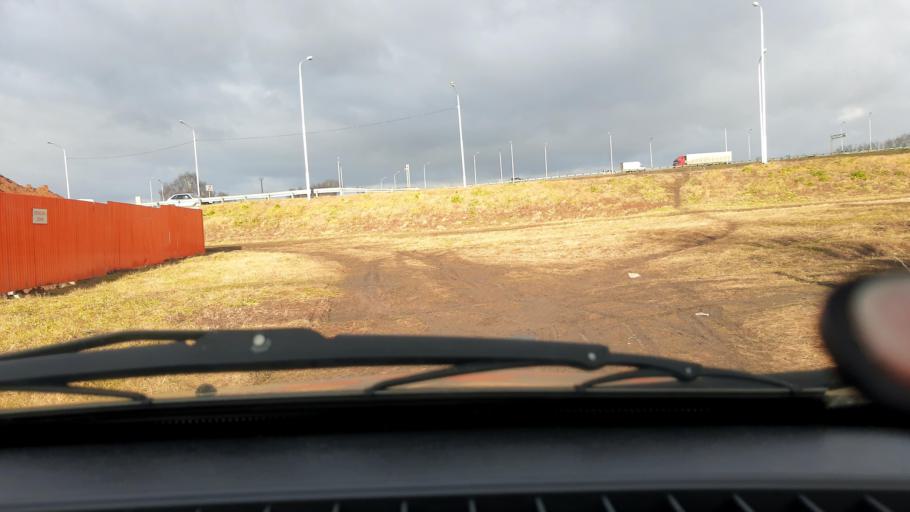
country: RU
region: Bashkortostan
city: Mikhaylovka
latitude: 54.7965
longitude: 55.8625
